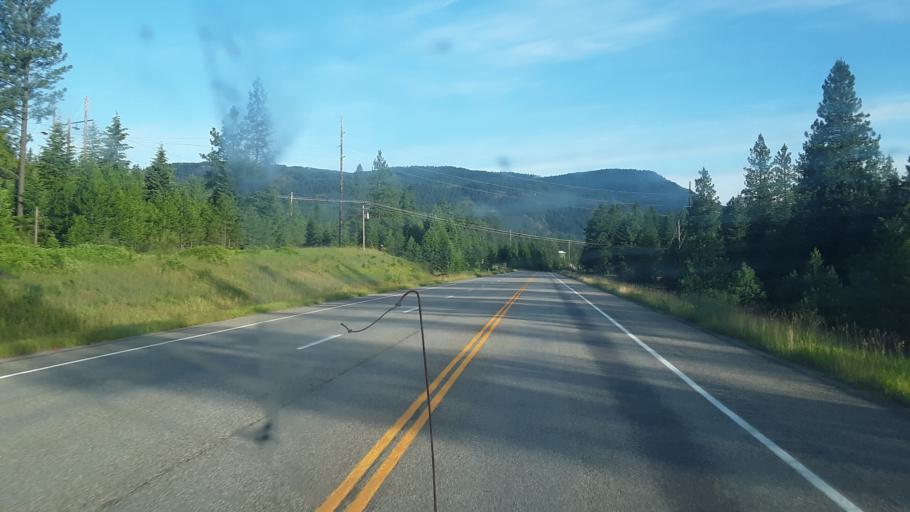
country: US
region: Montana
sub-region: Lincoln County
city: Libby
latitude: 48.4402
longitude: -115.8676
